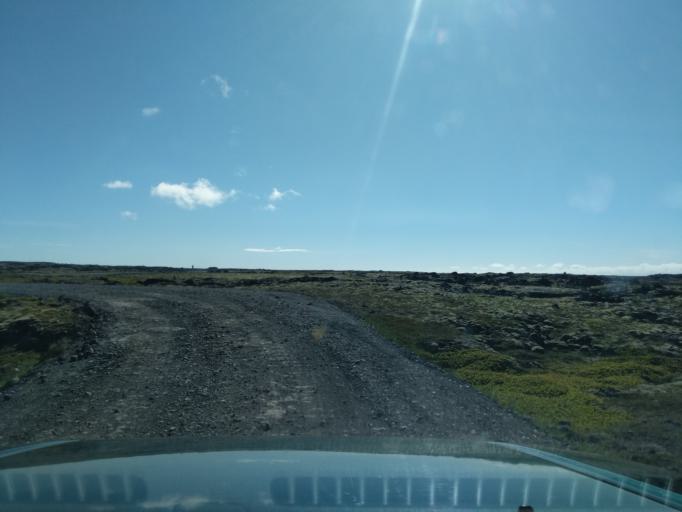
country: IS
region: West
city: Olafsvik
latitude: 64.8741
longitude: -24.0189
